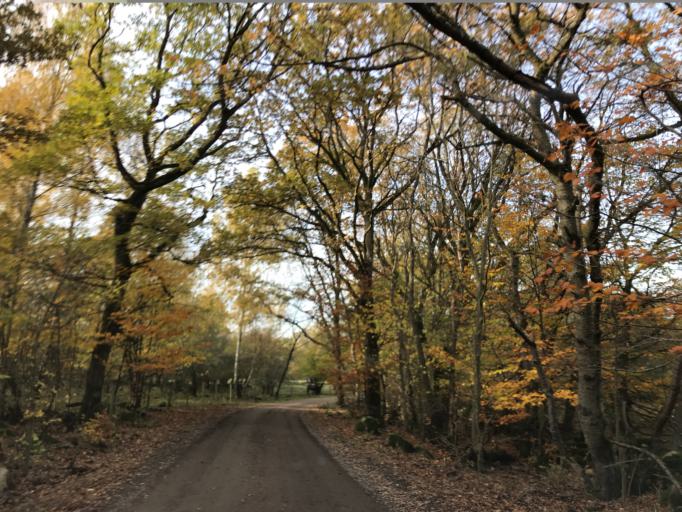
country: SE
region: Skane
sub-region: Bjuvs Kommun
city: Billesholm
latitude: 56.0649
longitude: 13.0219
